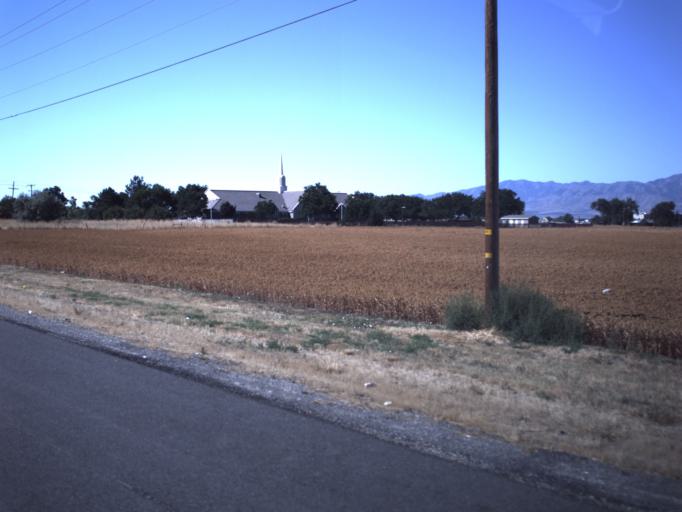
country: US
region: Utah
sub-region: Tooele County
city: Erda
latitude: 40.6044
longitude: -112.2944
